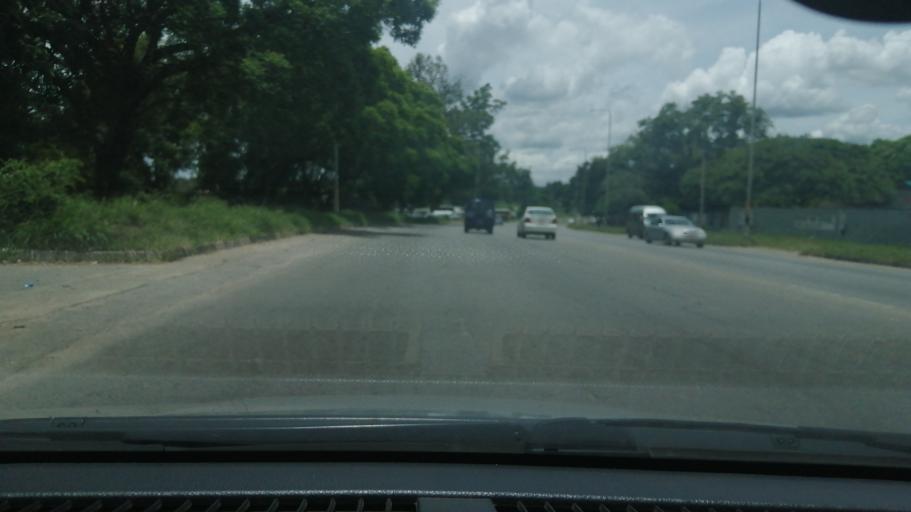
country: ZW
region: Harare
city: Harare
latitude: -17.8773
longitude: 31.0693
